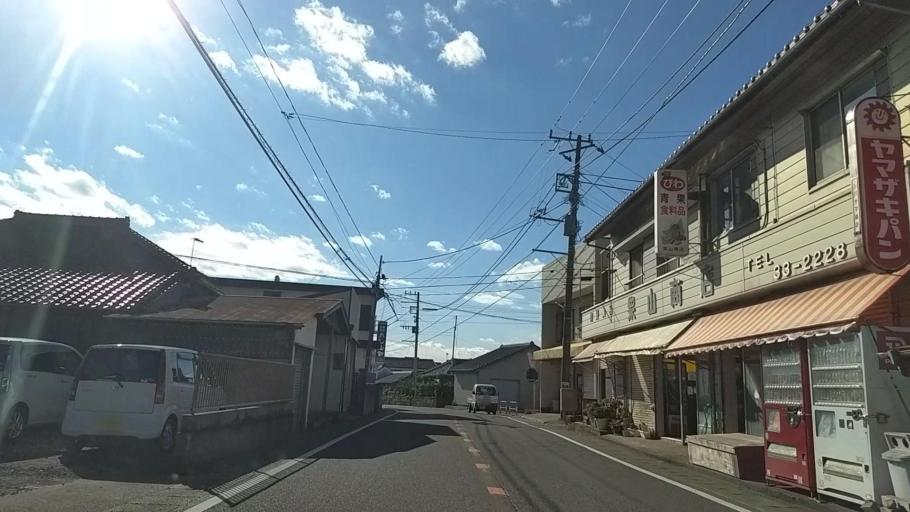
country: JP
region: Chiba
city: Tateyama
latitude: 35.0627
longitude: 139.8271
